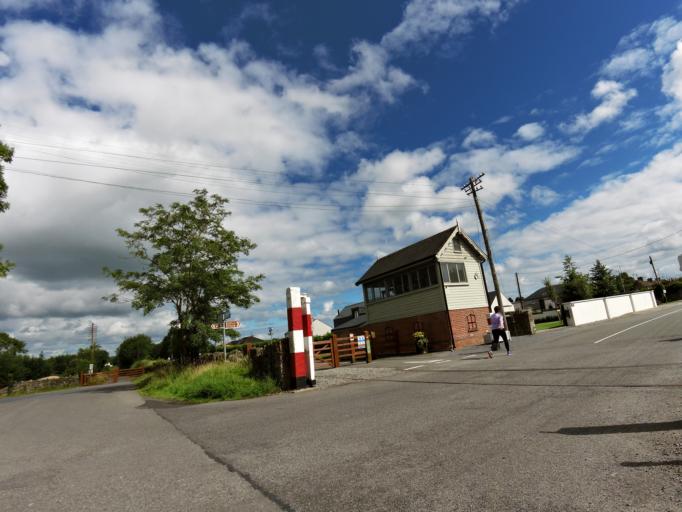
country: IE
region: Leinster
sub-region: An Iarmhi
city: Moate
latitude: 53.3994
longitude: -7.7237
